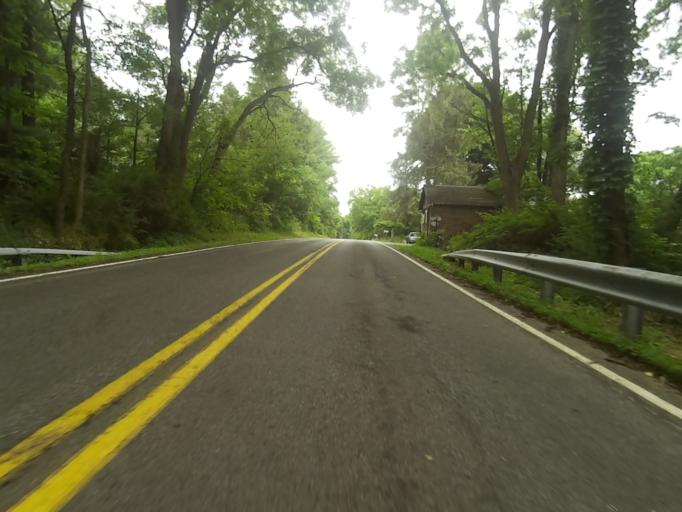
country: US
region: Pennsylvania
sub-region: Centre County
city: Stormstown
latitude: 40.7216
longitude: -77.9903
